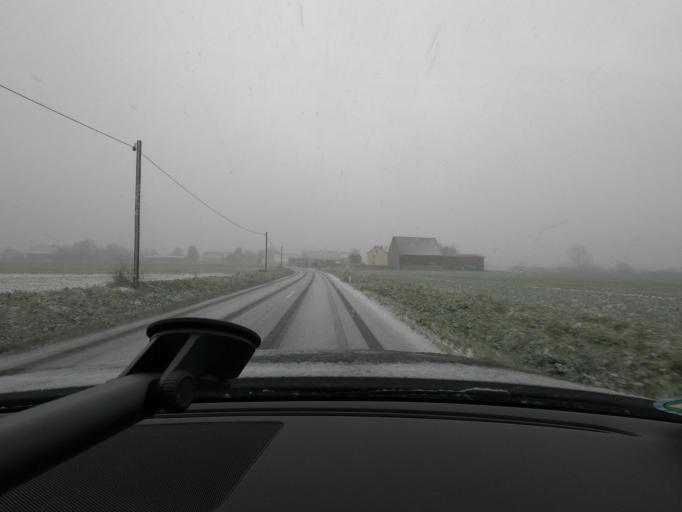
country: DE
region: North Rhine-Westphalia
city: Marsberg
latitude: 51.5181
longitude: 8.8582
